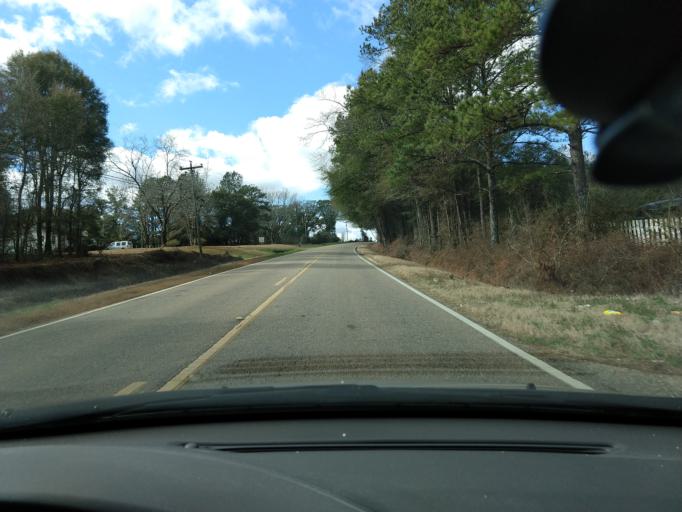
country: US
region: Alabama
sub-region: Coffee County
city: Enterprise
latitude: 31.3139
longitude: -85.9235
